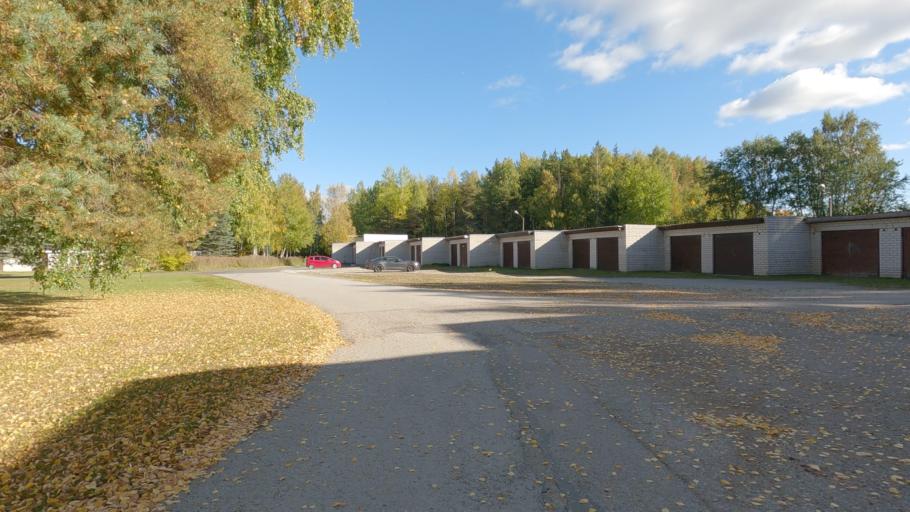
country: EE
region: Raplamaa
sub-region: Rapla vald
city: Rapla
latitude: 58.9950
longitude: 24.8066
